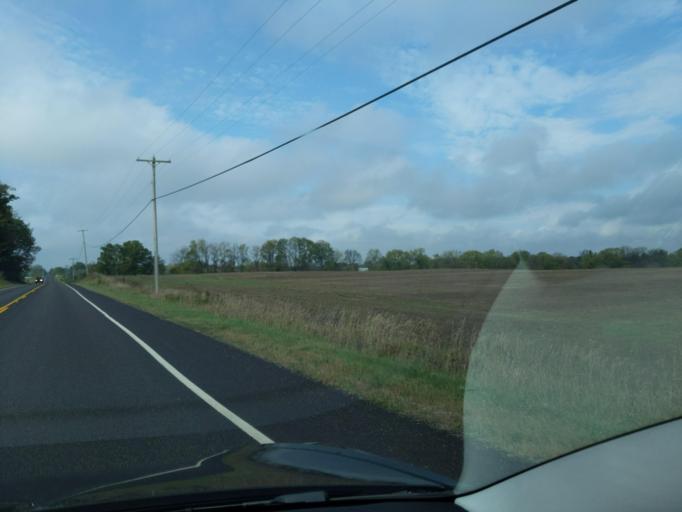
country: US
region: Michigan
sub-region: Eaton County
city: Potterville
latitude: 42.6257
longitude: -84.7214
